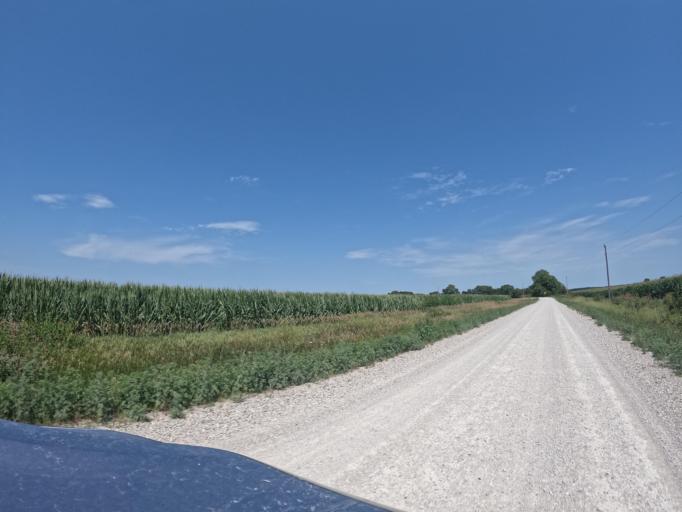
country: US
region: Iowa
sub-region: Henry County
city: Mount Pleasant
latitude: 40.8901
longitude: -91.6337
